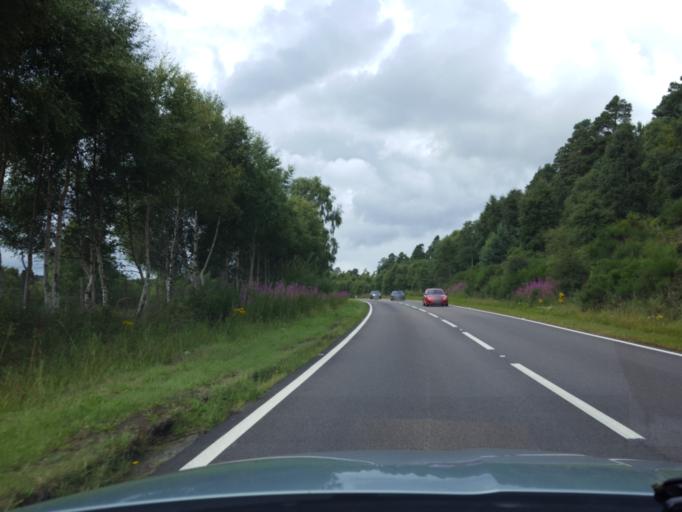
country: GB
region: Scotland
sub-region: Highland
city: Grantown on Spey
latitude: 57.2815
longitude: -3.6791
